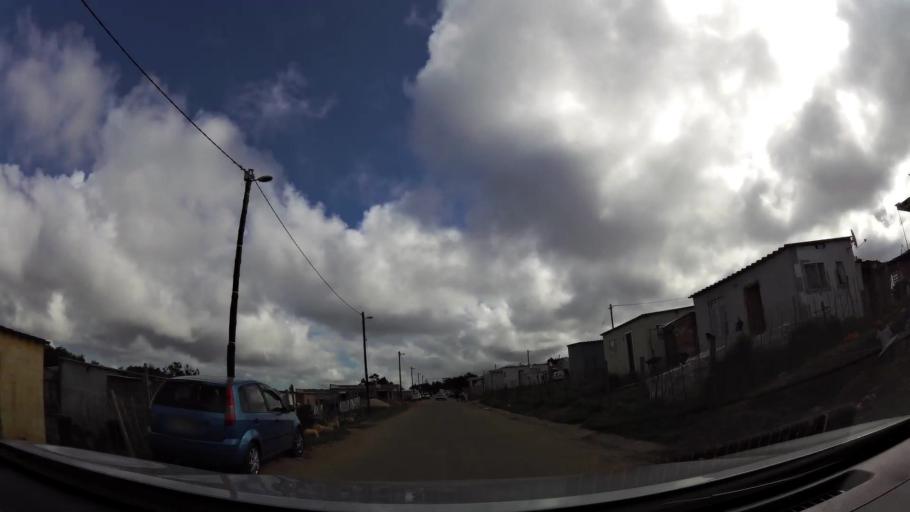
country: ZA
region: Western Cape
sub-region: Eden District Municipality
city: Plettenberg Bay
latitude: -34.0555
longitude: 23.3113
